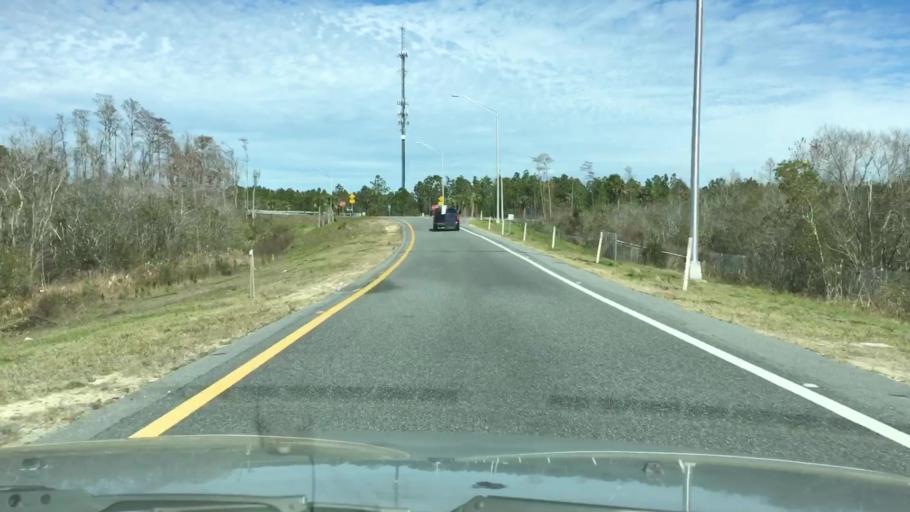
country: US
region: Florida
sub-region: Flagler County
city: Palm Coast
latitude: 29.5984
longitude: -81.2461
